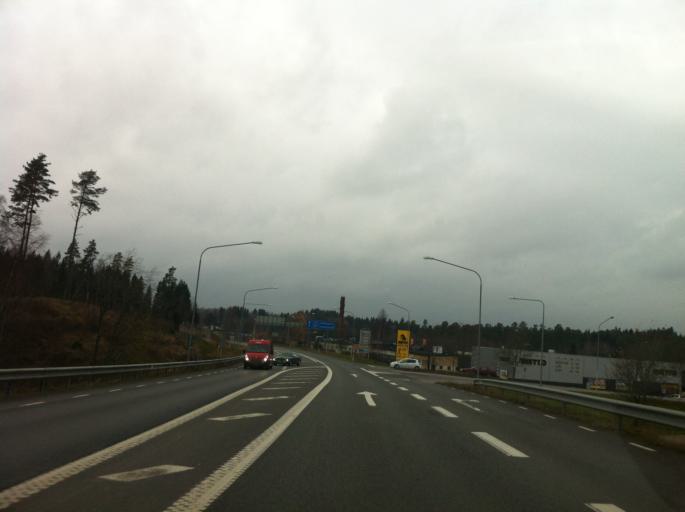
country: SE
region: Joenkoeping
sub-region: Savsjo Kommun
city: Saevsjoe
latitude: 57.3941
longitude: 14.6889
